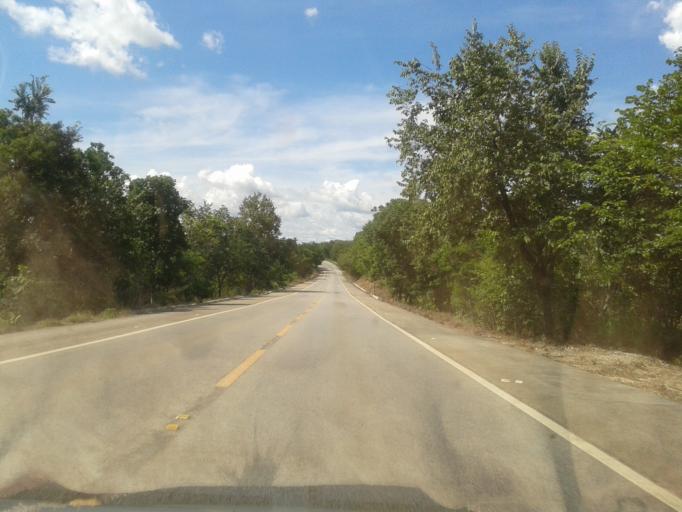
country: BR
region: Goias
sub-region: Goias
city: Goias
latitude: -15.7215
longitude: -50.1876
